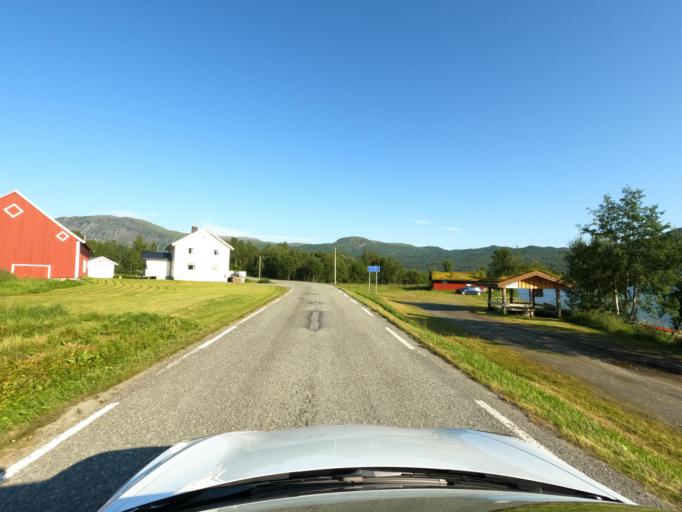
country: NO
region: Troms
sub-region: Gratangen
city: Gratangen
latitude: 68.5615
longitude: 17.6894
